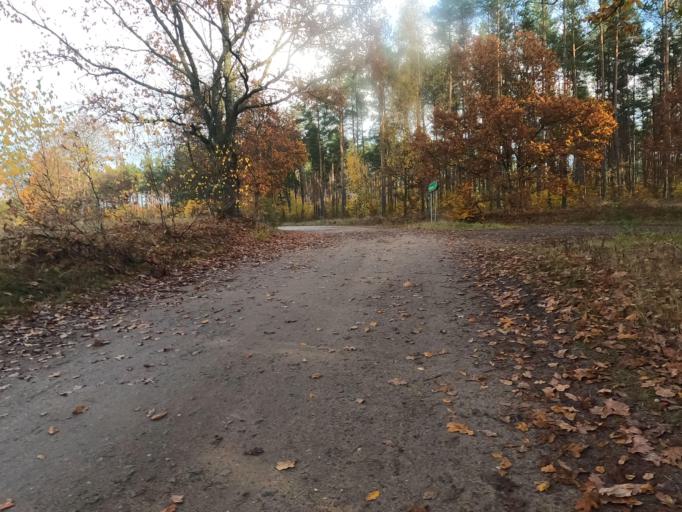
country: PL
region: West Pomeranian Voivodeship
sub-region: Powiat szczecinecki
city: Borne Sulinowo
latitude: 53.5300
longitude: 16.4617
